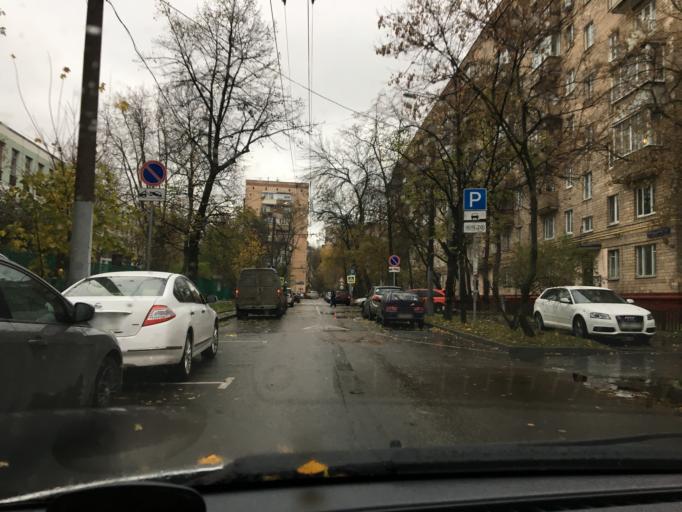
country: RU
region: Moskovskaya
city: Dorogomilovo
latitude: 55.7720
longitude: 37.5821
